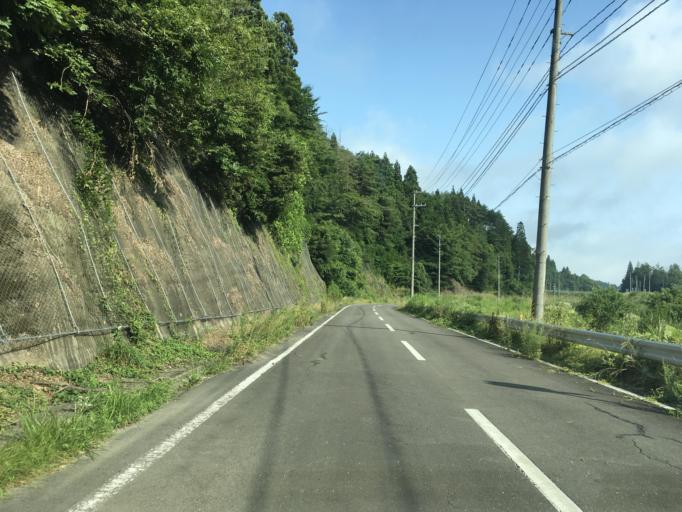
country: JP
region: Iwate
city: Ofunato
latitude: 38.9067
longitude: 141.6222
